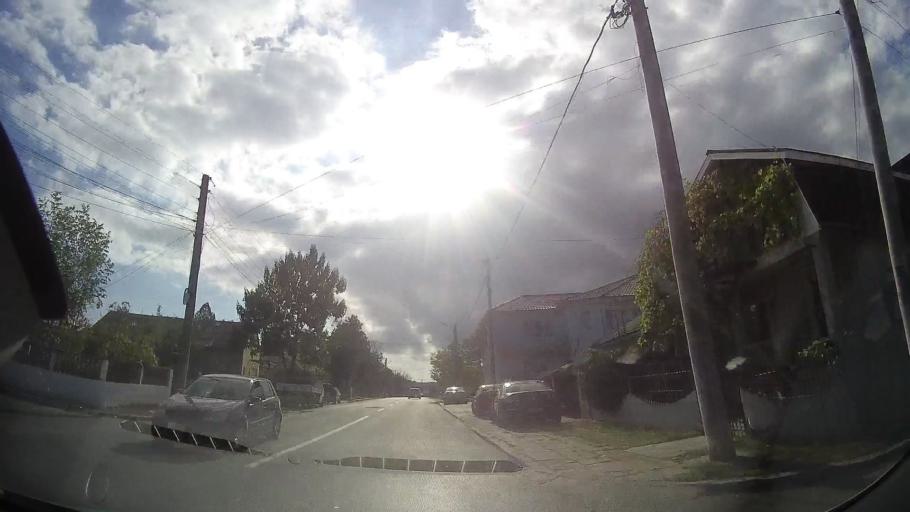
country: RO
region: Constanta
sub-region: Oras Techirghiol
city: Techirghiol
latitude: 44.0609
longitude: 28.5992
